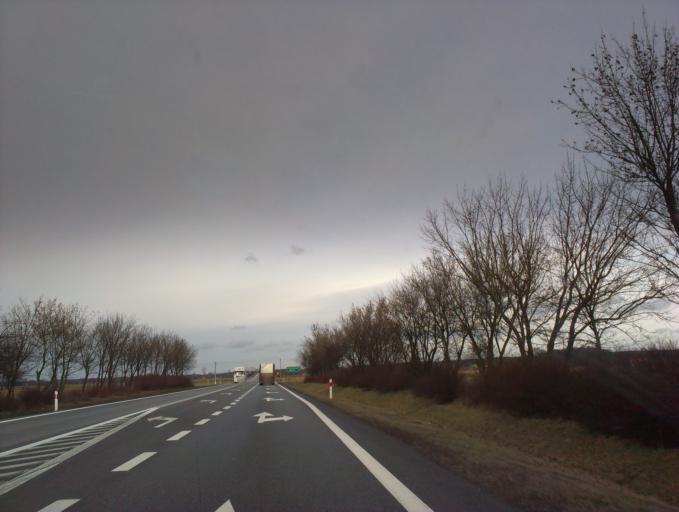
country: PL
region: Kujawsko-Pomorskie
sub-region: Powiat lipnowski
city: Skepe
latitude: 52.8656
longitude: 19.3135
